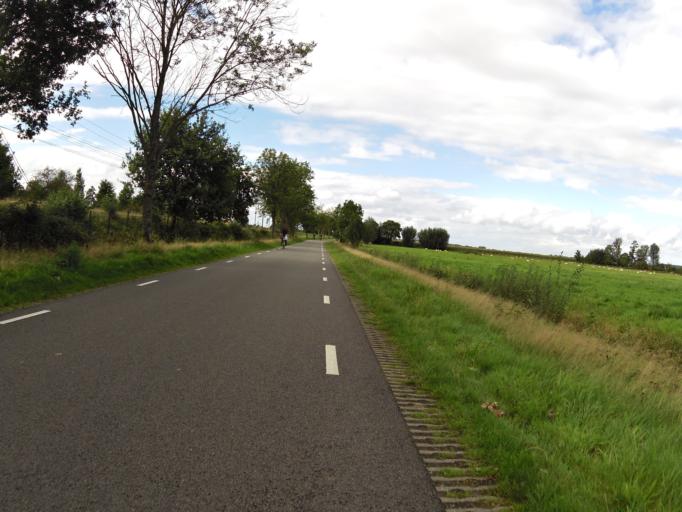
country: NL
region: Utrecht
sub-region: Gemeente Soest
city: Soest
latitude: 52.1791
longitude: 5.3236
